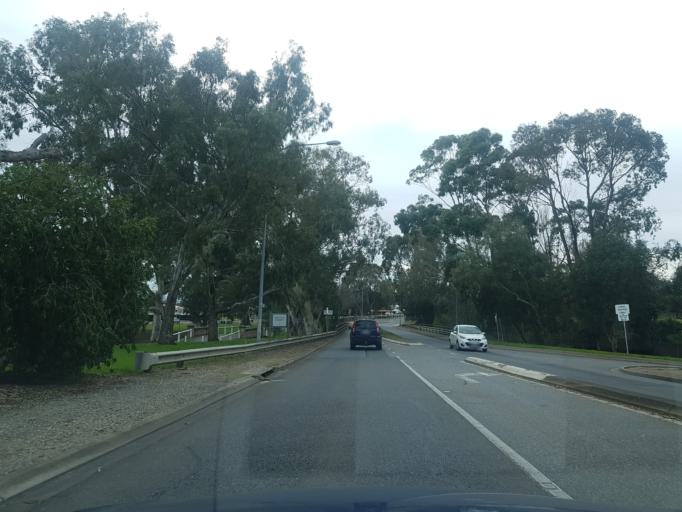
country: AU
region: South Australia
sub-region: Mitcham
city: Mitcham
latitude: -34.9814
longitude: 138.6219
